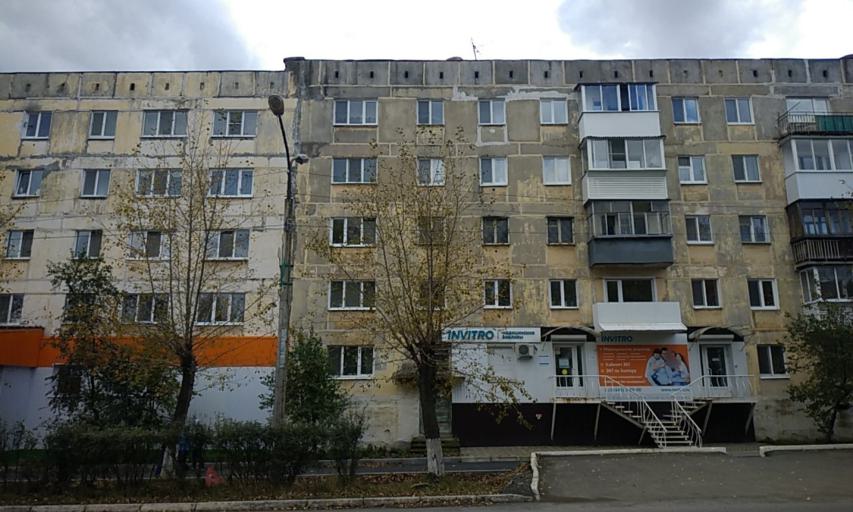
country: RU
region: Sverdlovsk
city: Krasnoural'sk
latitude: 58.3588
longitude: 60.0294
